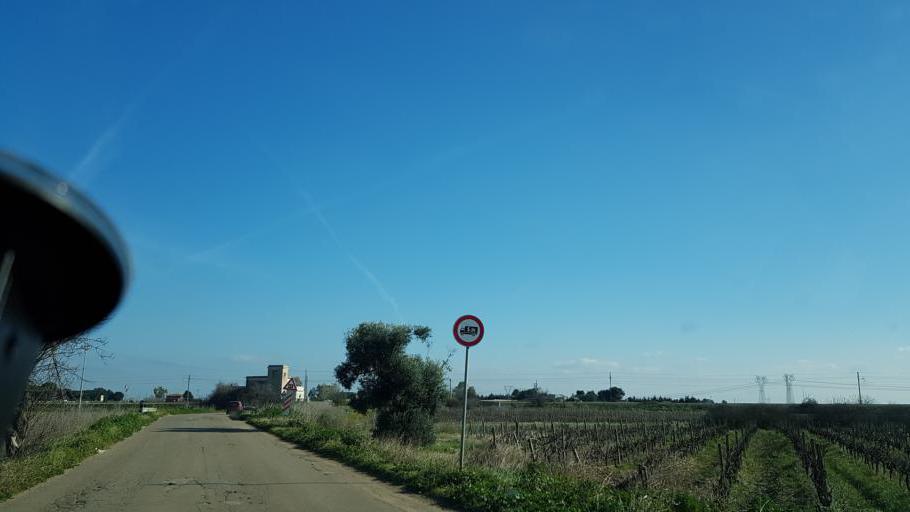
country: IT
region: Apulia
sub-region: Provincia di Brindisi
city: Brindisi
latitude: 40.6081
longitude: 17.8762
